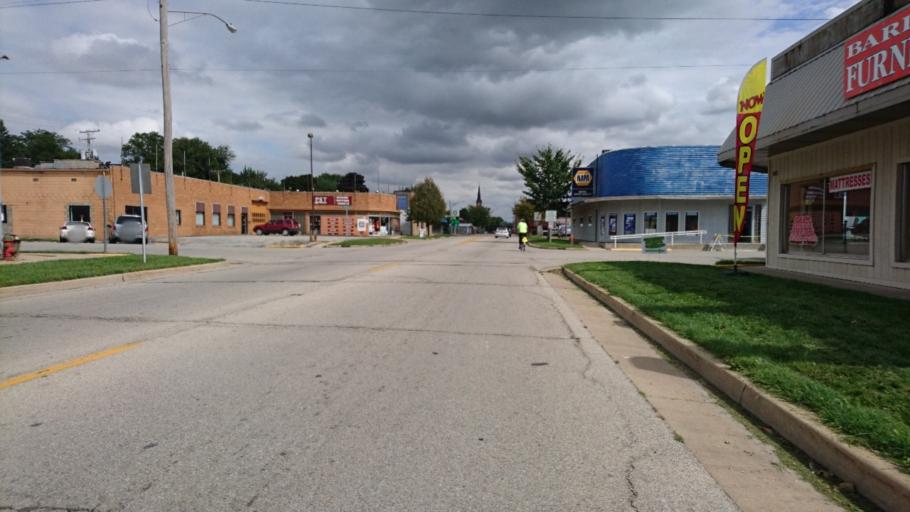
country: US
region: Illinois
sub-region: Livingston County
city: Pontiac
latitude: 40.8810
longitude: -88.6337
